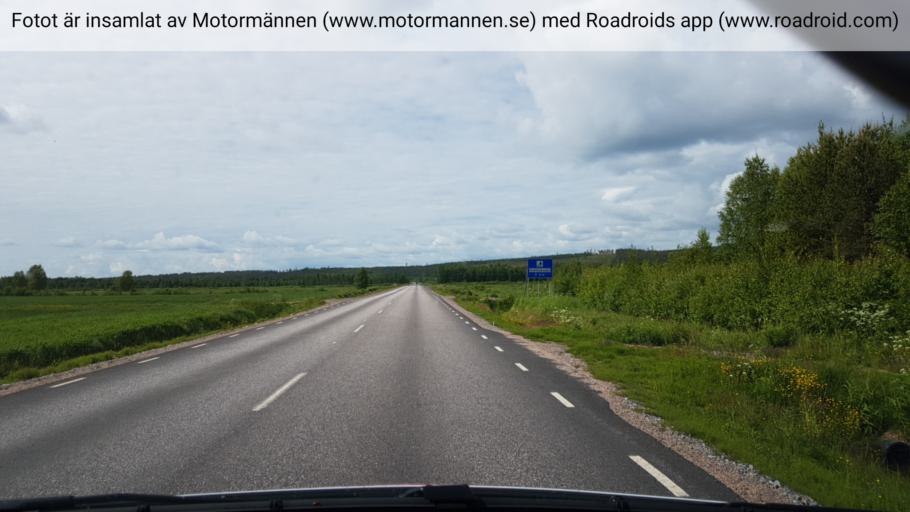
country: SE
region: Norrbotten
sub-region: Overtornea Kommun
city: OEvertornea
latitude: 66.5524
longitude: 23.8067
